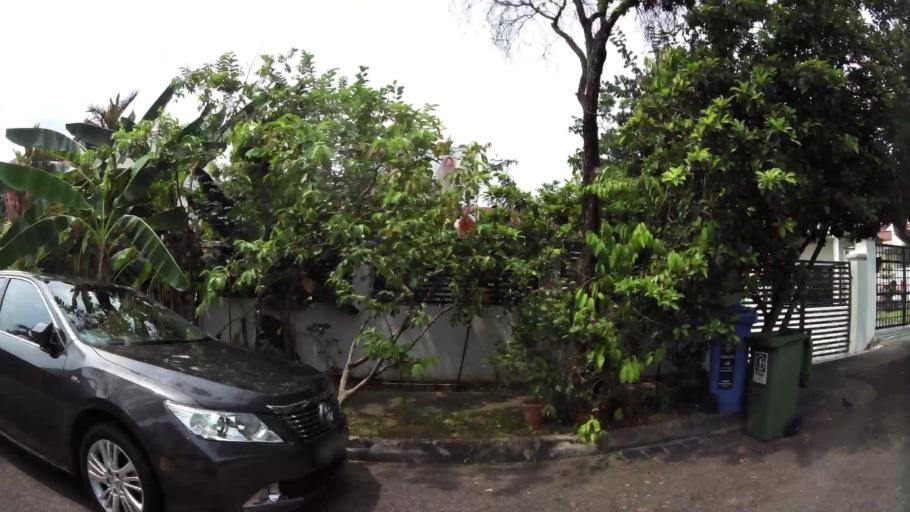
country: SG
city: Singapore
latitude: 1.3432
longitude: 103.7741
